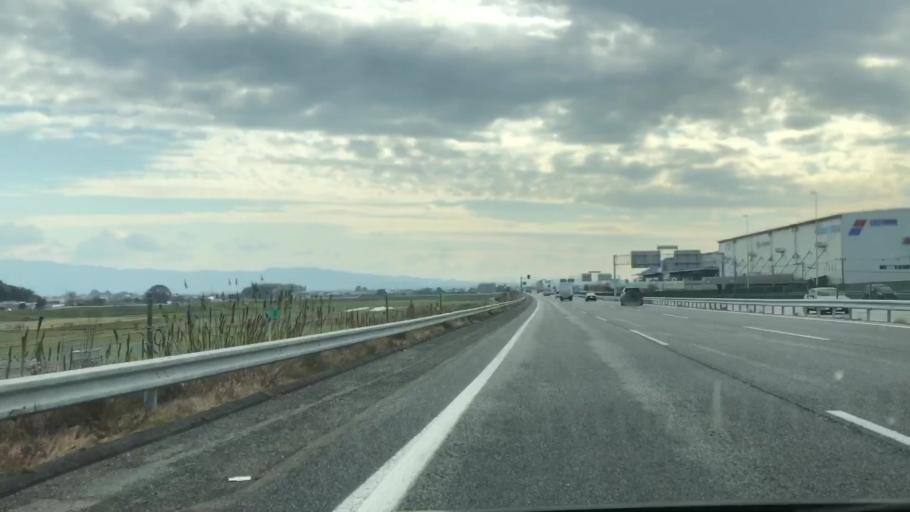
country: JP
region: Saga Prefecture
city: Tosu
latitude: 33.3918
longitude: 130.5384
